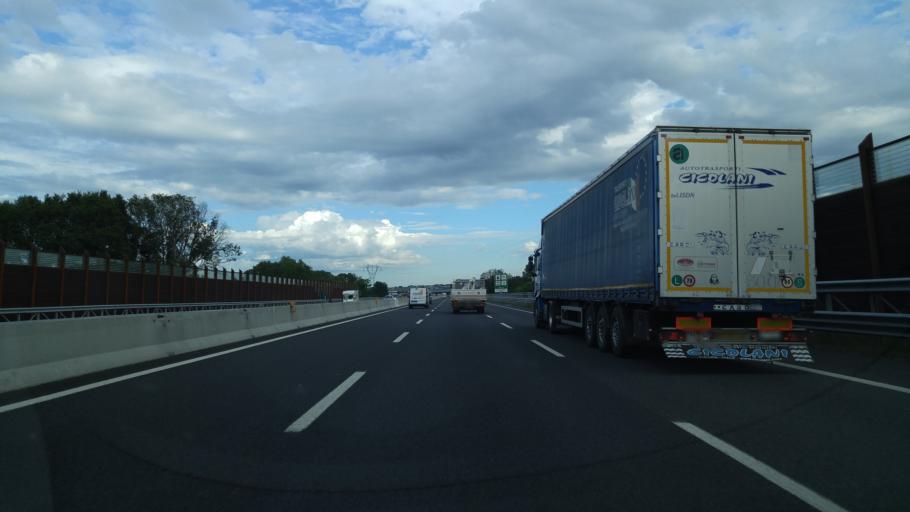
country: IT
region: Emilia-Romagna
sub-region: Provincia di Rimini
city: Coriano
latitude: 43.9988
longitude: 12.6107
